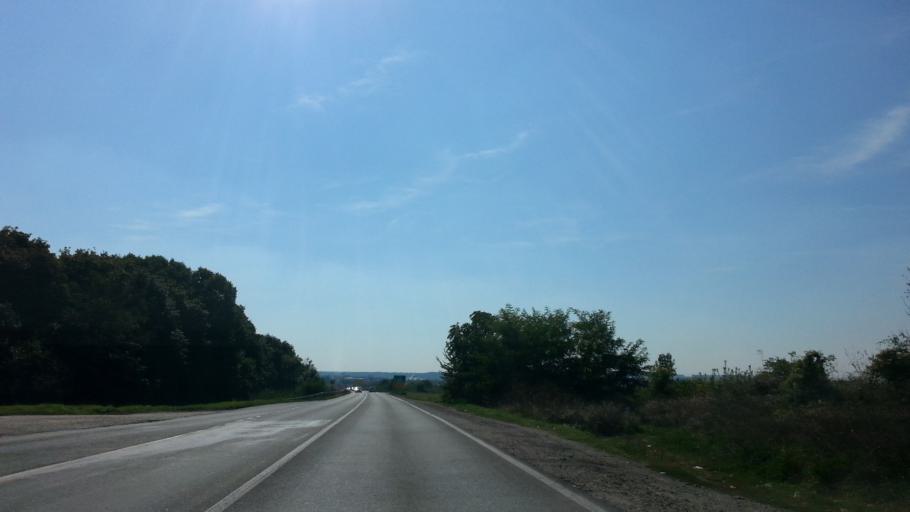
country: RS
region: Central Serbia
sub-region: Belgrade
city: Rakovica
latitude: 44.7219
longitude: 20.4170
